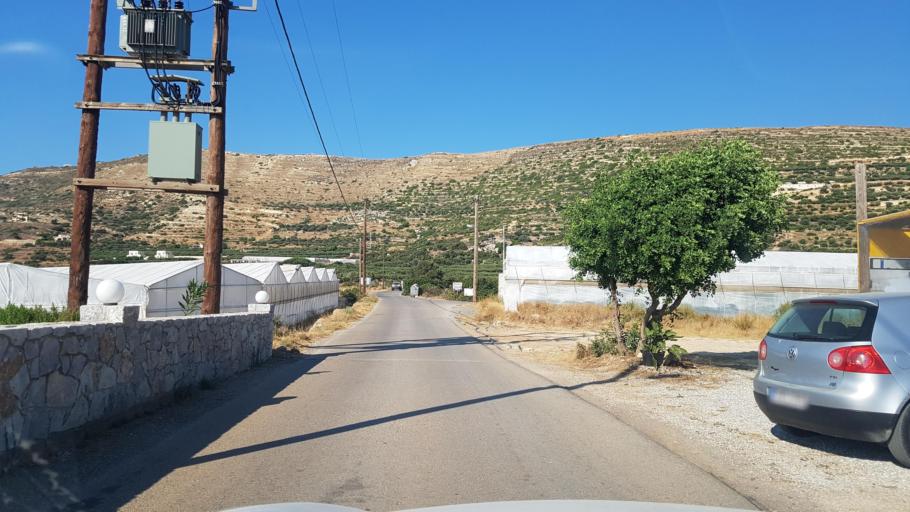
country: GR
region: Crete
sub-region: Nomos Chanias
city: Platanos
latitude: 35.4904
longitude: 23.5857
